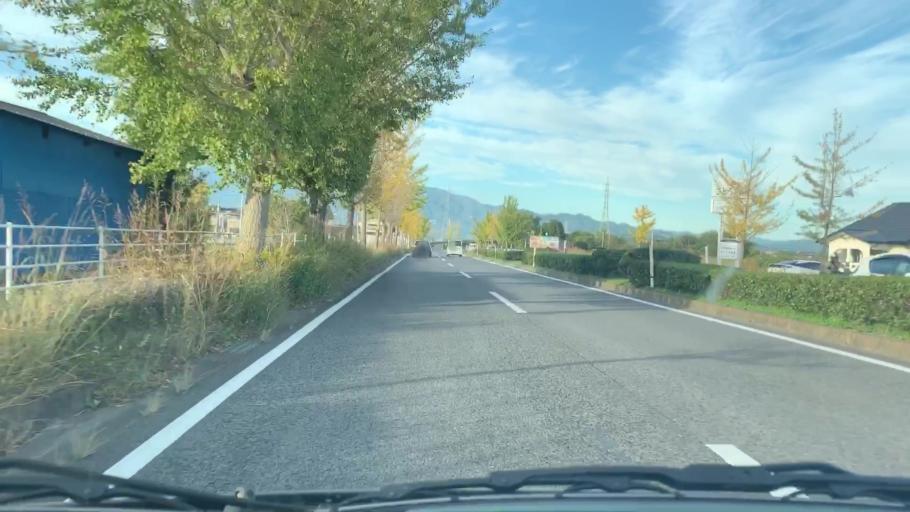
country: JP
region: Saga Prefecture
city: Saga-shi
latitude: 33.2520
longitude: 130.1989
